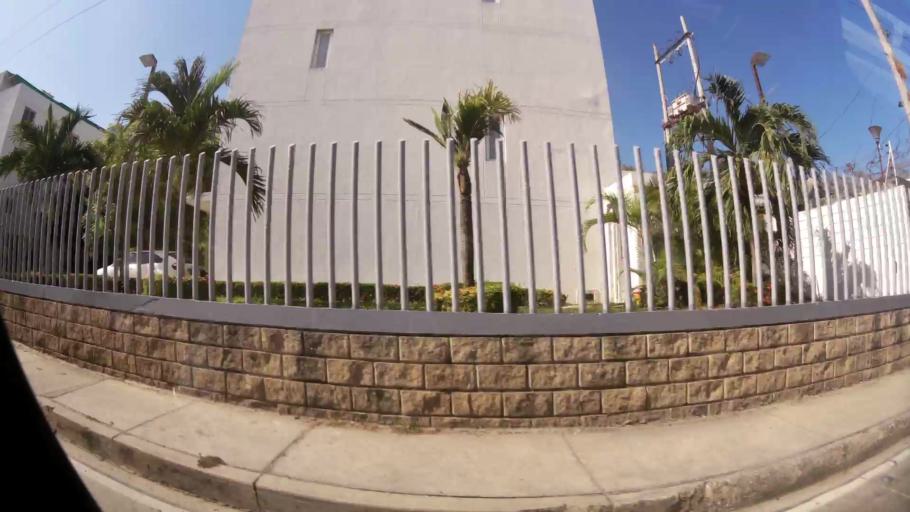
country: CO
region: Bolivar
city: Cartagena
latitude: 10.3888
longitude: -75.4682
